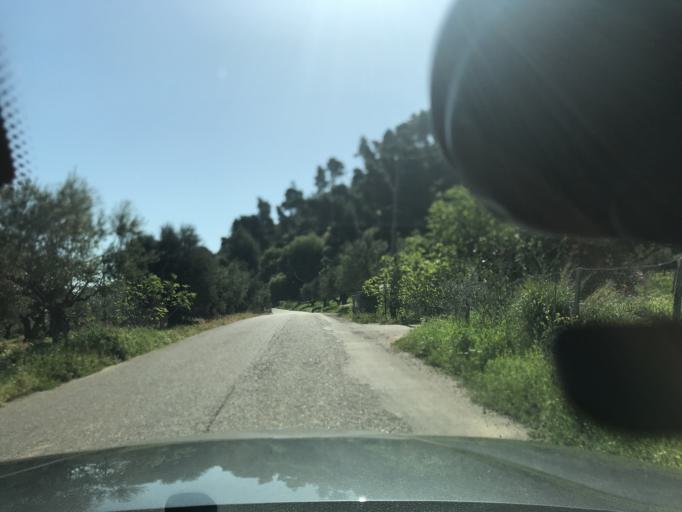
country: GR
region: West Greece
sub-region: Nomos Ileias
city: Alfiousa
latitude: 37.6405
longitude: 21.5251
